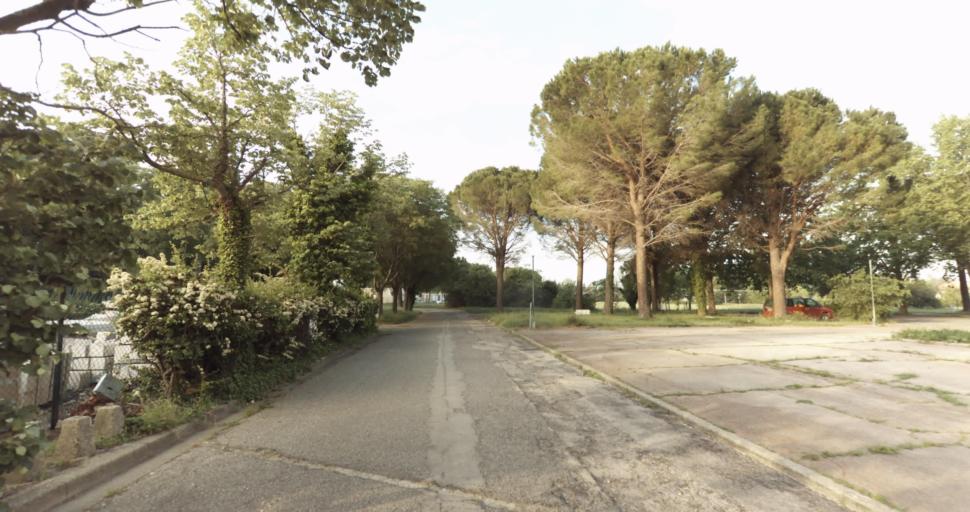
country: FR
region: Languedoc-Roussillon
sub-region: Departement du Gard
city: Caissargues
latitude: 43.8227
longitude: 4.3876
